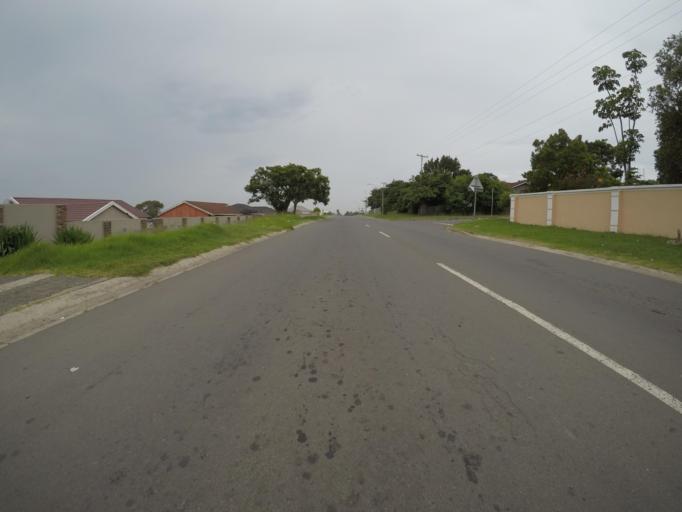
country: ZA
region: Eastern Cape
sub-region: Buffalo City Metropolitan Municipality
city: East London
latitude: -32.9992
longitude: 27.8514
